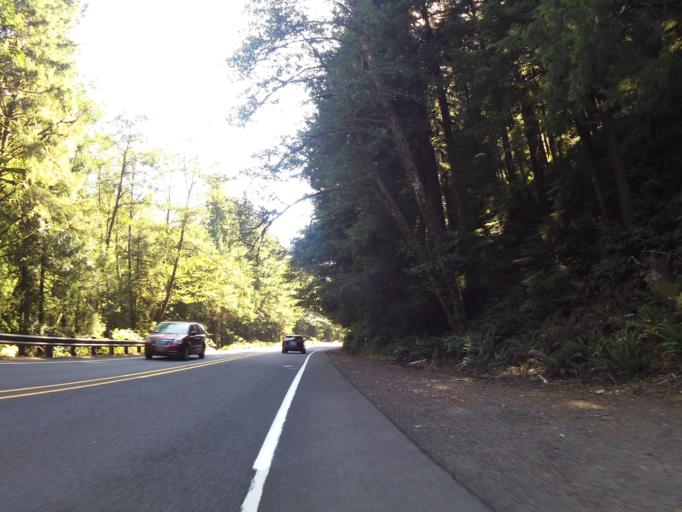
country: US
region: Oregon
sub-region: Clatsop County
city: Cannon Beach
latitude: 45.7660
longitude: -123.9518
